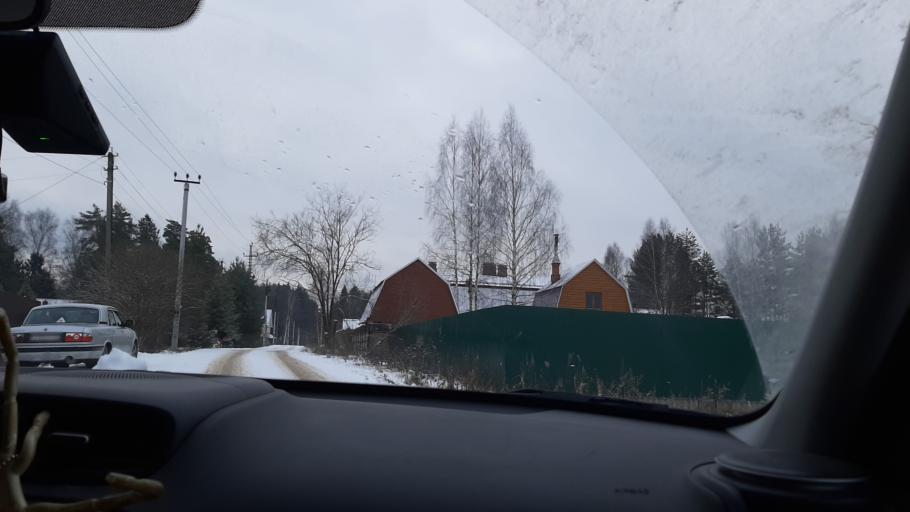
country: RU
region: Ivanovo
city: Kokhma
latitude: 56.9014
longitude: 41.0073
